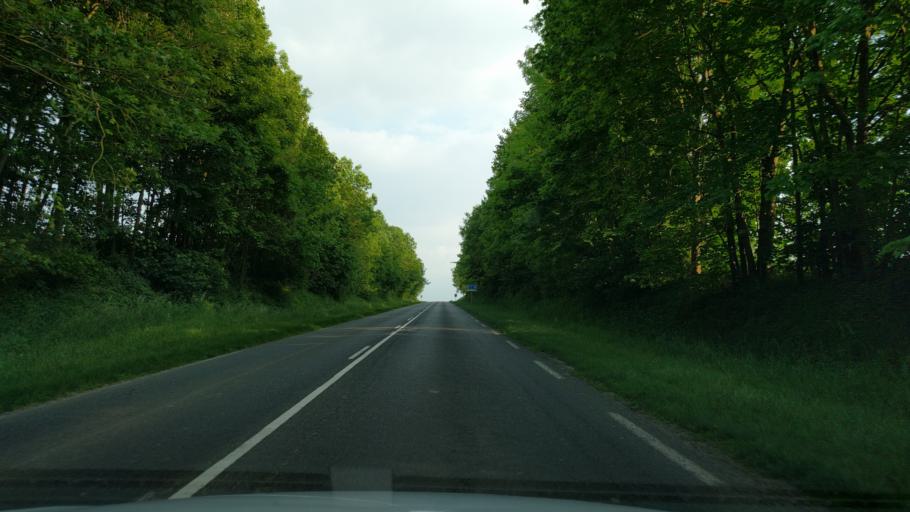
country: FR
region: Picardie
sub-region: Departement de la Somme
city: Peronne
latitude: 49.9772
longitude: 2.9182
